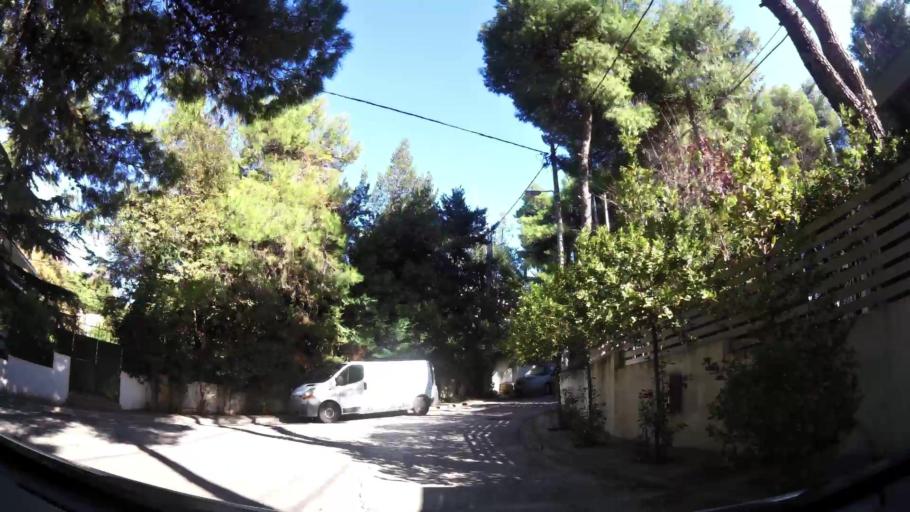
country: GR
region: Attica
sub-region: Nomarchia Athinas
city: Ekali
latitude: 38.1149
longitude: 23.8489
